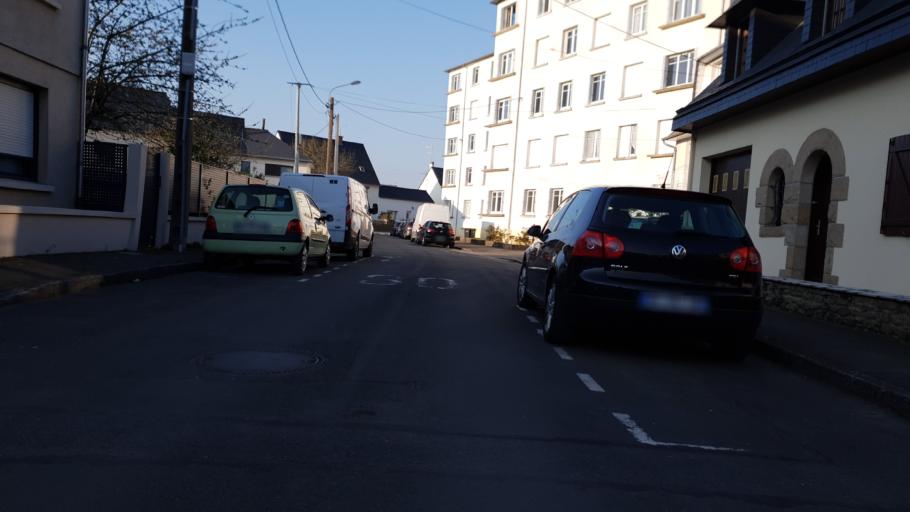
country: FR
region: Brittany
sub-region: Departement d'Ille-et-Vilaine
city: Rennes
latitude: 48.1023
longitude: -1.7023
